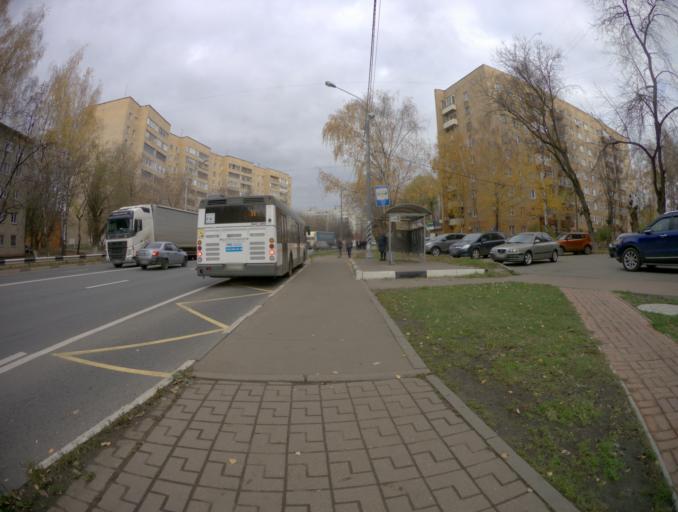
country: RU
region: Moskovskaya
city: Orekhovo-Zuyevo
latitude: 55.8064
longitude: 38.9682
